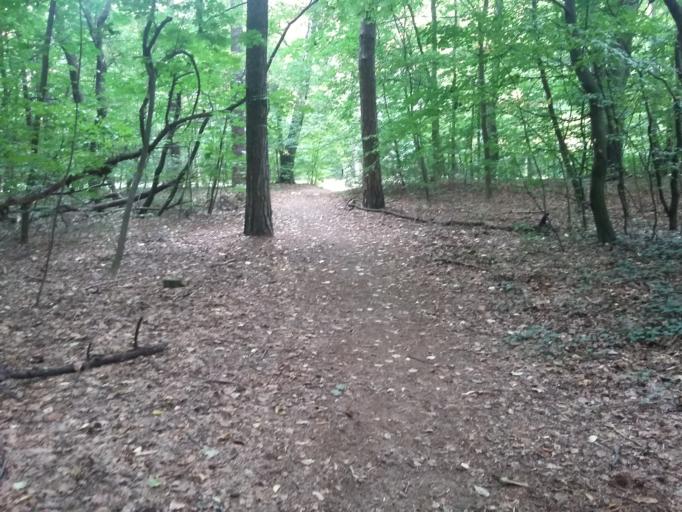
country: PL
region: Lodz Voivodeship
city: Lodz
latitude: 51.7617
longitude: 19.4183
